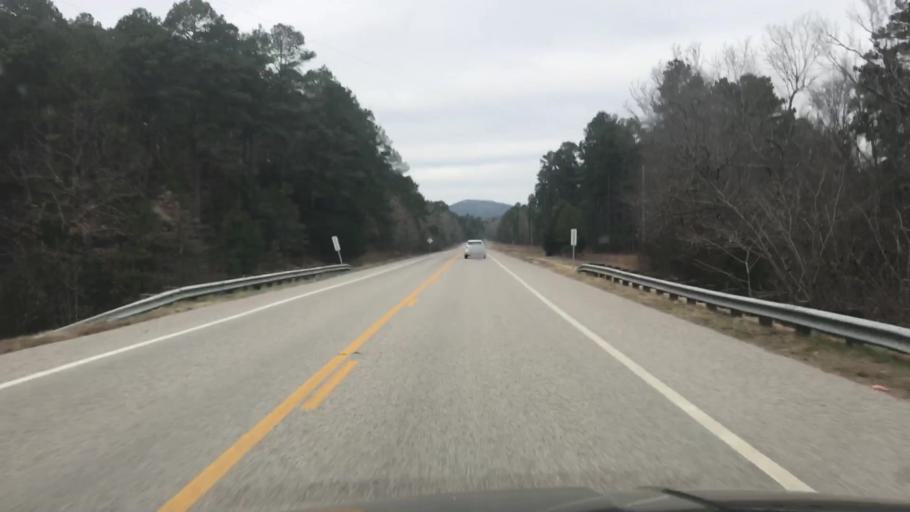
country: US
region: Arkansas
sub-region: Scott County
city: Waldron
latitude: 34.7113
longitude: -93.9404
